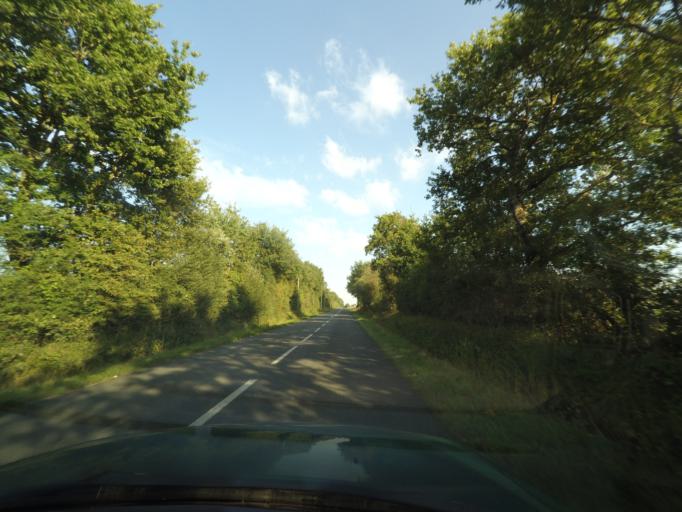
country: FR
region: Pays de la Loire
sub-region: Departement de la Loire-Atlantique
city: La Limouziniere
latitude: 47.0215
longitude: -1.6059
